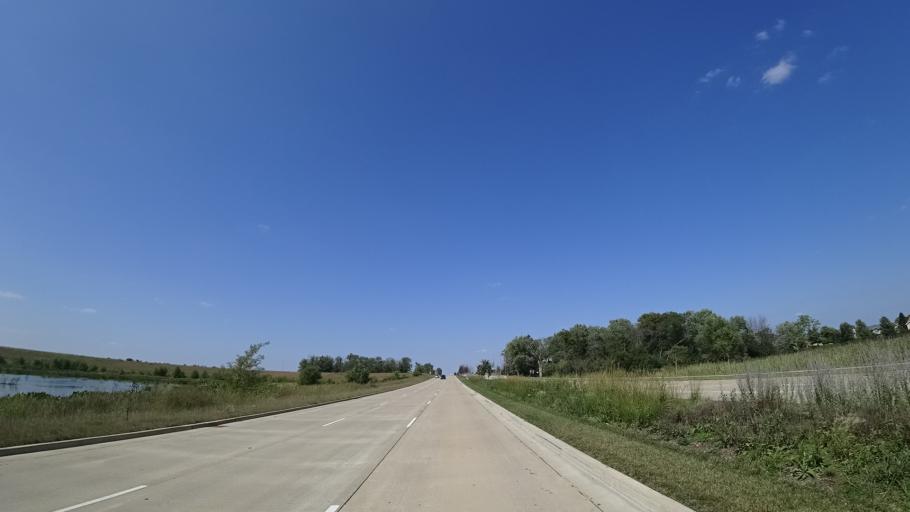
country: US
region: Illinois
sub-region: Cook County
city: Orland Hills
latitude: 41.5700
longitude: -87.8517
